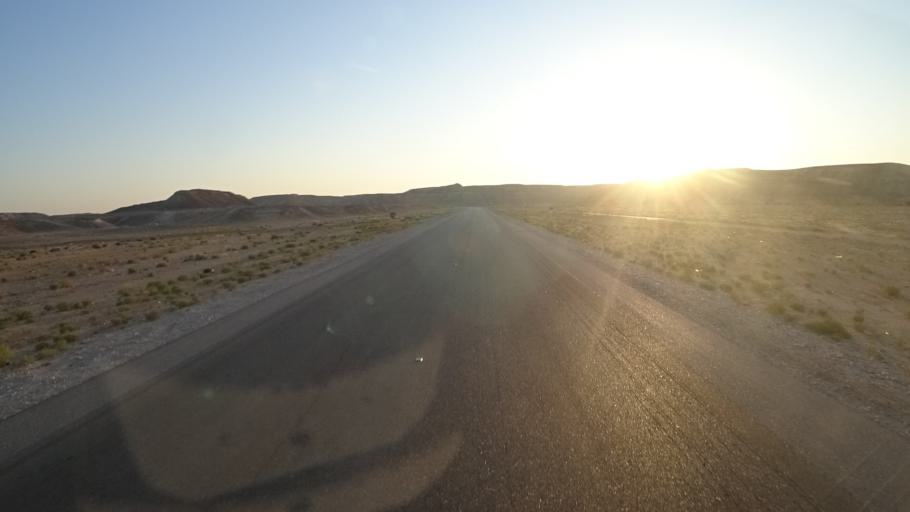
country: OM
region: Zufar
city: Salalah
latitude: 17.5091
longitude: 53.3676
